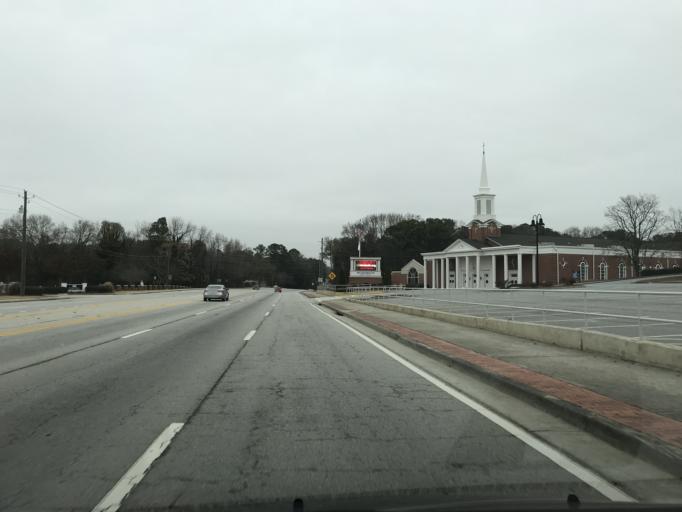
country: US
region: Georgia
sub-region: DeKalb County
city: Clarkston
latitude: 33.8292
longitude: -84.2491
